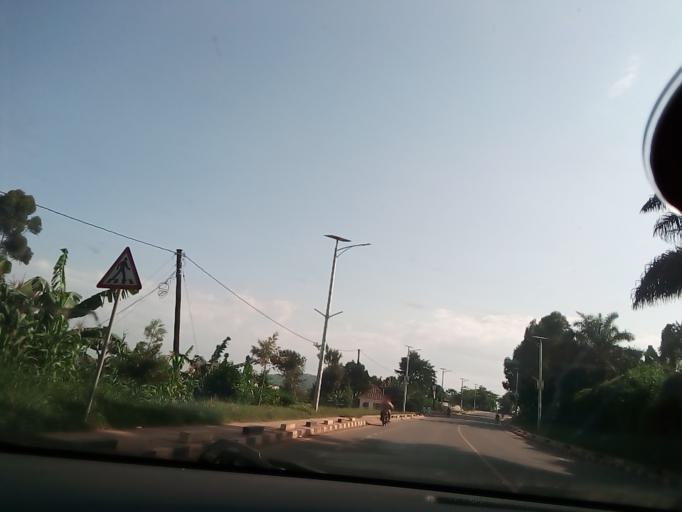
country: UG
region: Central Region
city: Masaka
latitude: -0.3262
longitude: 31.7379
